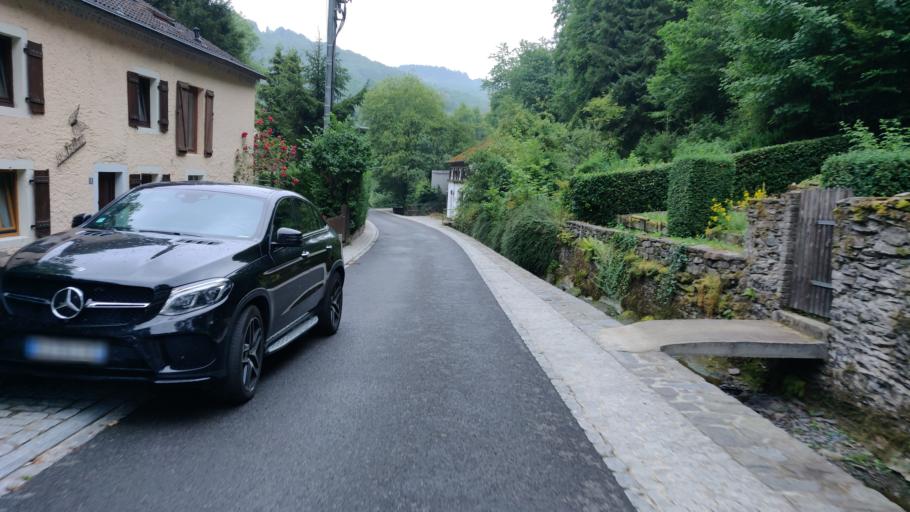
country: LU
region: Diekirch
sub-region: Canton de Wiltz
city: Goesdorf
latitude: 49.9035
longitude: 5.9610
